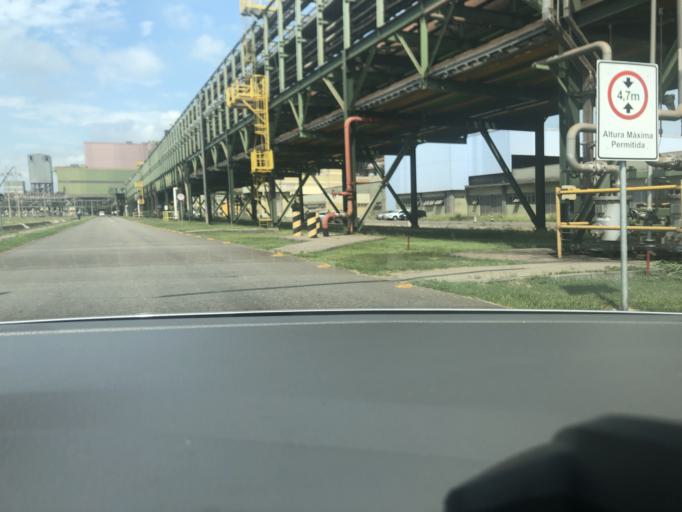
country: BR
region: Rio de Janeiro
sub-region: Itaguai
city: Itaguai
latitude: -22.9095
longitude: -43.7441
